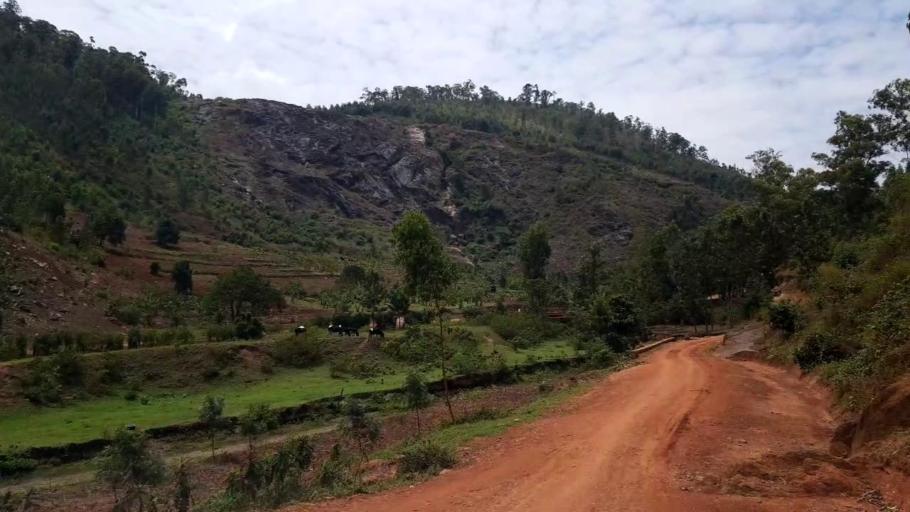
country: RW
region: Northern Province
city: Byumba
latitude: -1.5132
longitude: 30.1931
